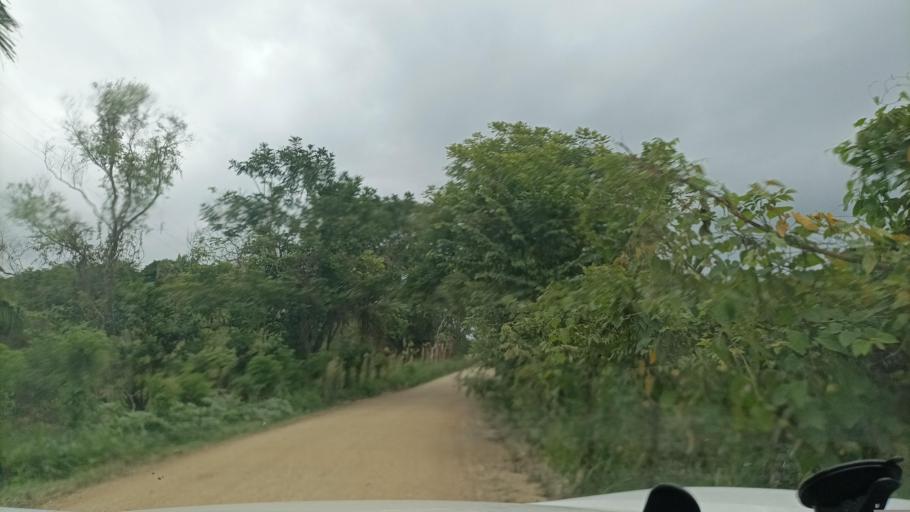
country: MX
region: Veracruz
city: Hidalgotitlan
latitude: 17.6495
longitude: -94.5014
